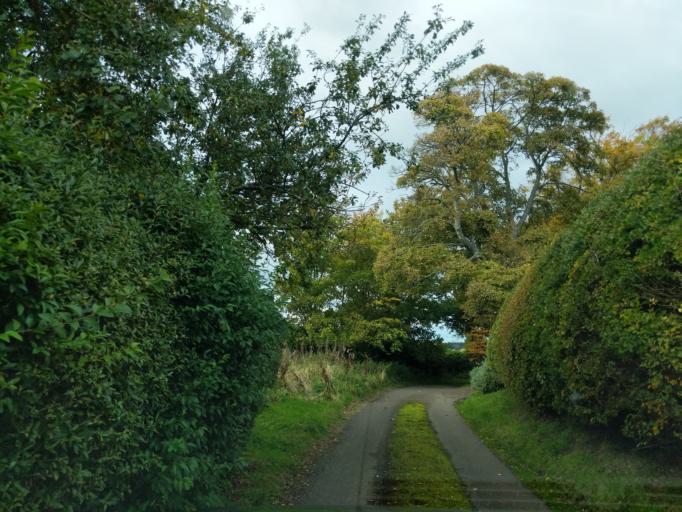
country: GB
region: Scotland
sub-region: East Lothian
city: Haddington
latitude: 55.9428
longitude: -2.7132
